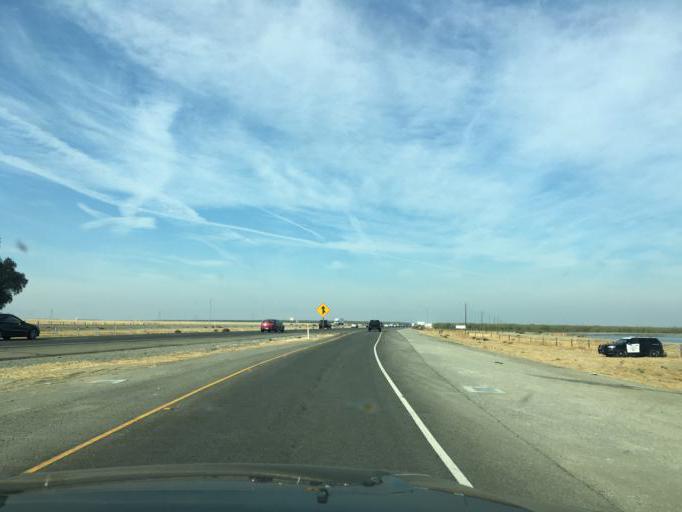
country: US
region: California
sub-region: Kings County
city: Avenal
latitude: 36.0906
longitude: -120.1152
